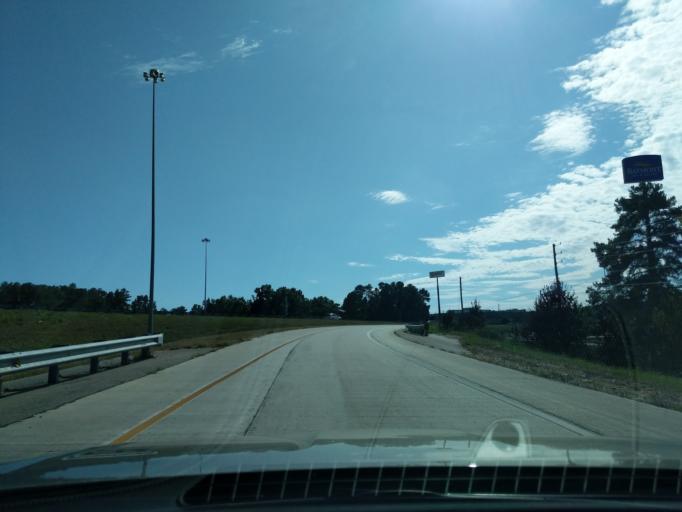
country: US
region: Georgia
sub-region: Columbia County
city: Martinez
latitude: 33.4938
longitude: -82.0863
